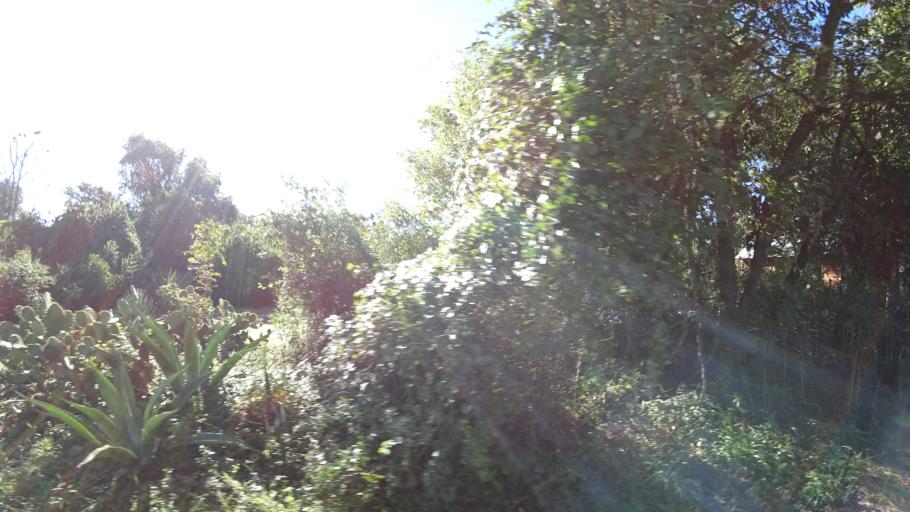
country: US
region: Texas
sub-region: Travis County
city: Hornsby Bend
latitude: 30.2283
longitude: -97.6646
